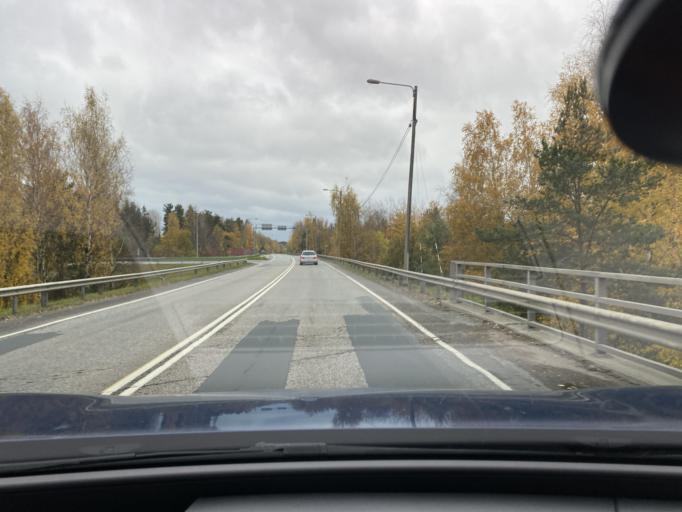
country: FI
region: Satakunta
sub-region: Rauma
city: Rauma
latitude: 61.1324
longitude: 21.5342
